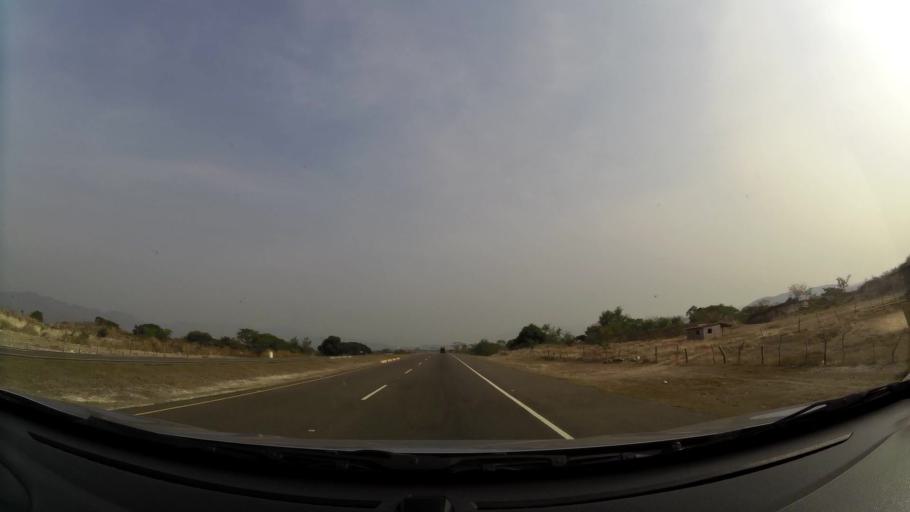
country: HN
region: Comayagua
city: Comayagua
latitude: 14.4519
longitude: -87.6639
